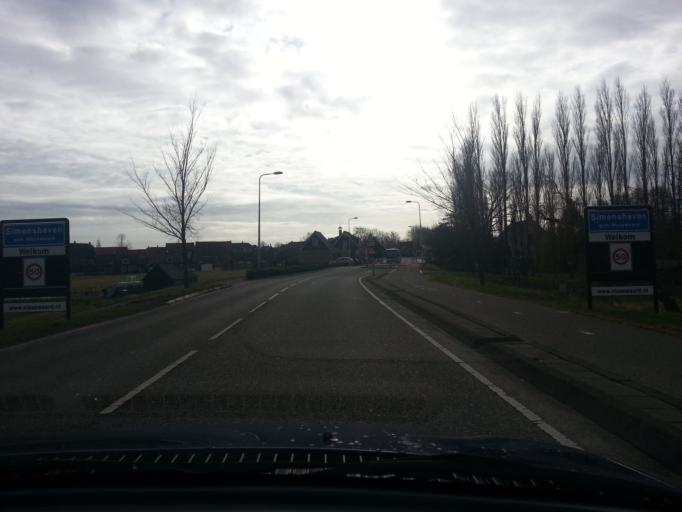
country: NL
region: South Holland
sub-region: Gemeente Spijkenisse
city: Spijkenisse
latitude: 51.8239
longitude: 4.2860
